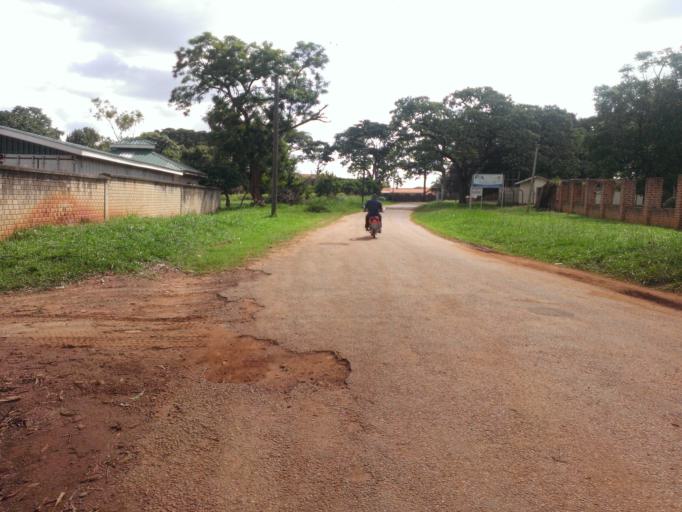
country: UG
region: Northern Region
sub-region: Gulu District
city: Gulu
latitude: 2.7808
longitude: 32.2999
